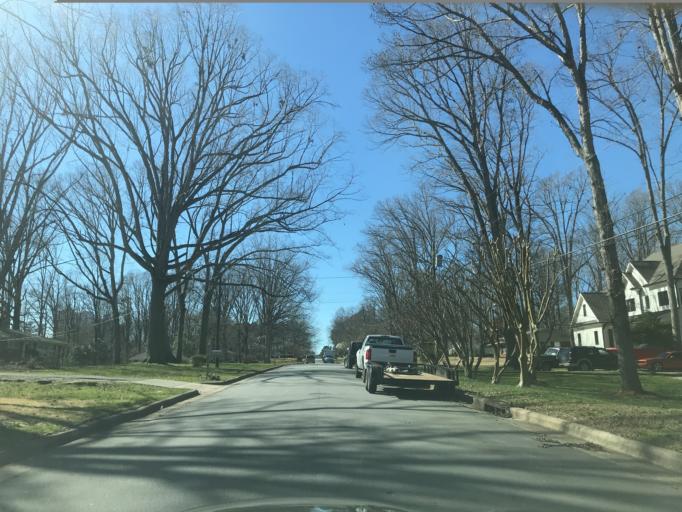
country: US
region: North Carolina
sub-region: Wake County
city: West Raleigh
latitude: 35.8476
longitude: -78.6387
